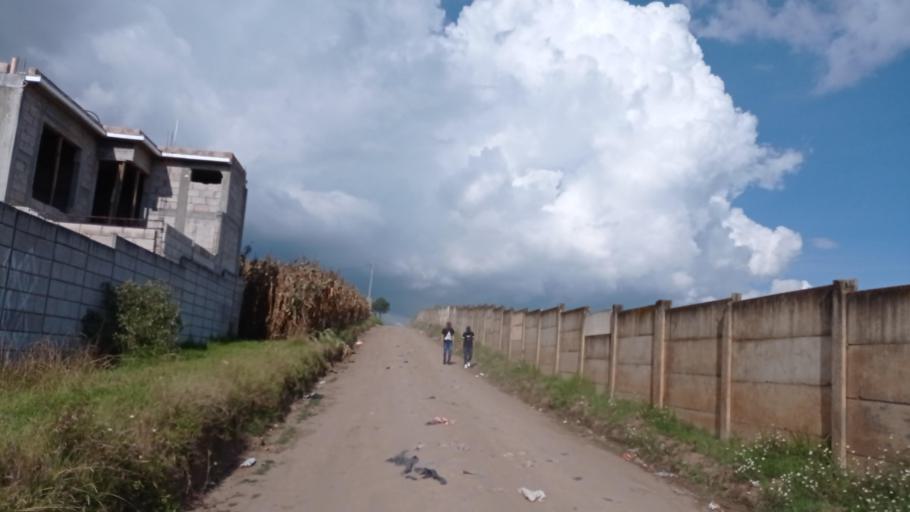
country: GT
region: Quetzaltenango
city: Olintepeque
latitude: 14.8676
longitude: -91.5018
